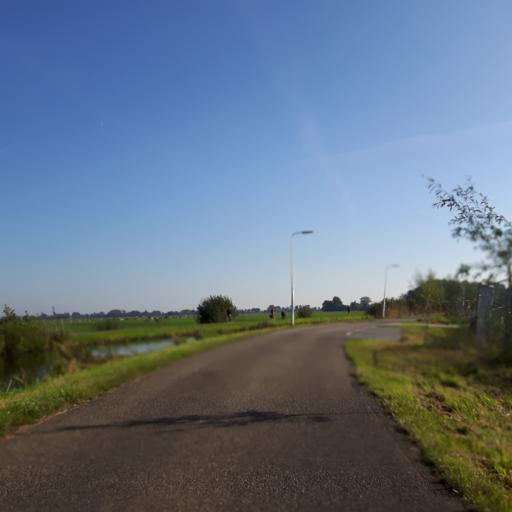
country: NL
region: South Holland
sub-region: Gemeente Schoonhoven
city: Schoonhoven
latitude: 51.9557
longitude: 4.8488
